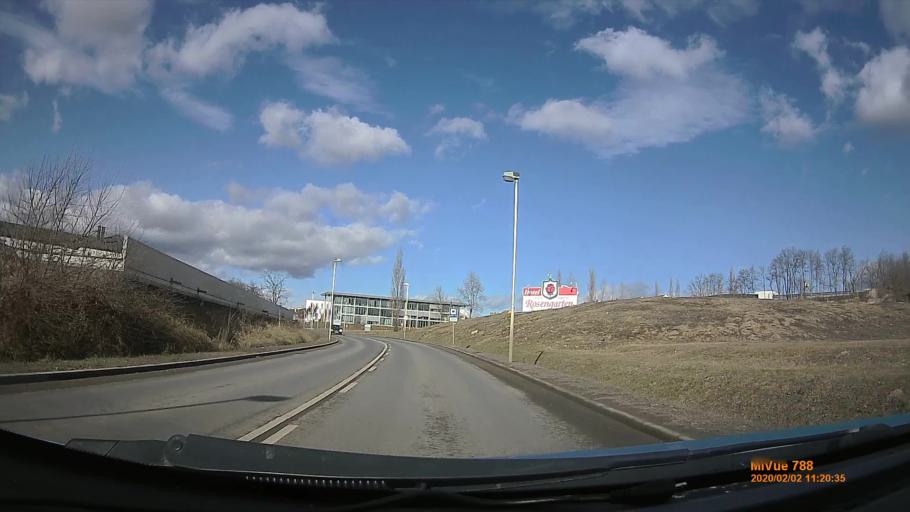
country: HU
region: Gyor-Moson-Sopron
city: Sopron
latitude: 47.6857
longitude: 16.6081
